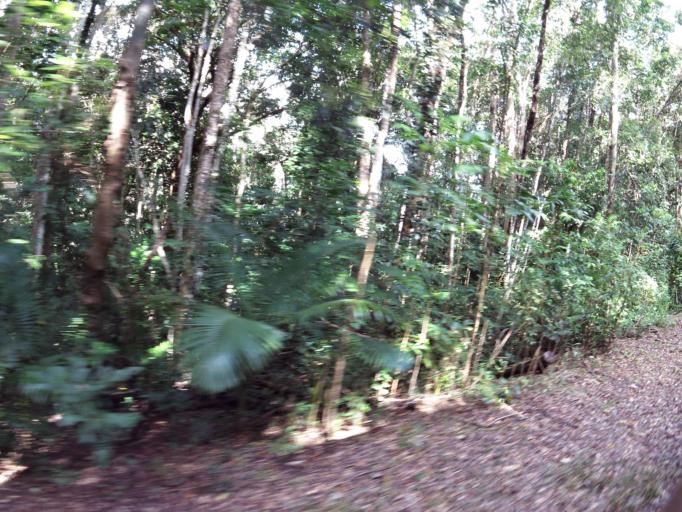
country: AU
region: Queensland
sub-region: Tablelands
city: Kuranda
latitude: -16.8262
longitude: 145.6391
